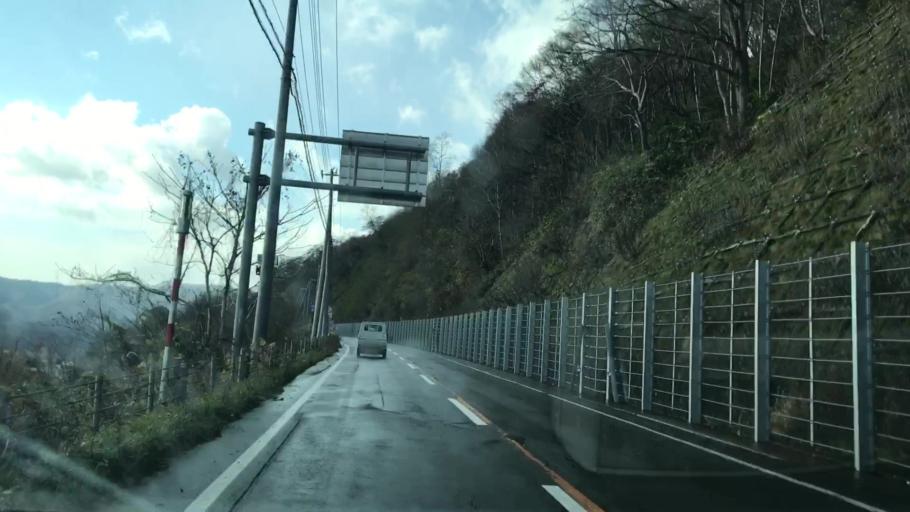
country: JP
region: Hokkaido
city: Yoichi
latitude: 43.2968
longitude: 140.5955
